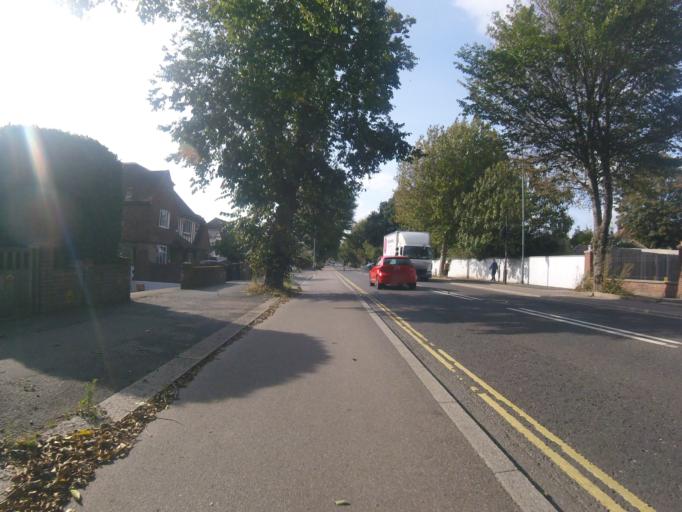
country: GB
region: England
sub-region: Brighton and Hove
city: Hove
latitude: 50.8365
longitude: -0.1630
